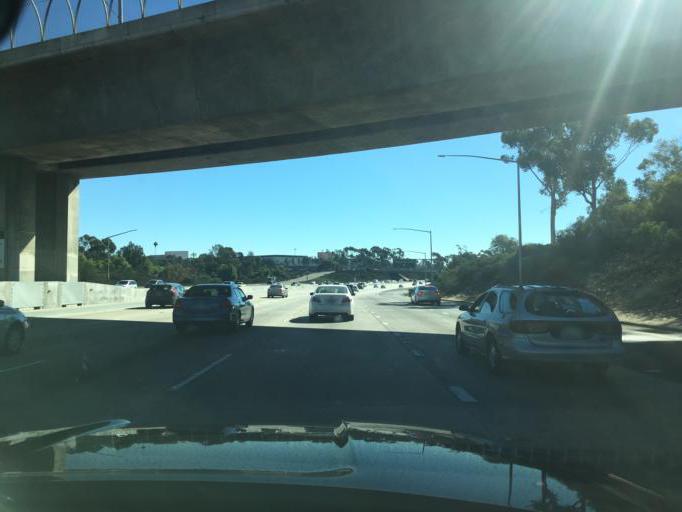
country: US
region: California
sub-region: San Diego County
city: National City
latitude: 32.7083
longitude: -117.0978
